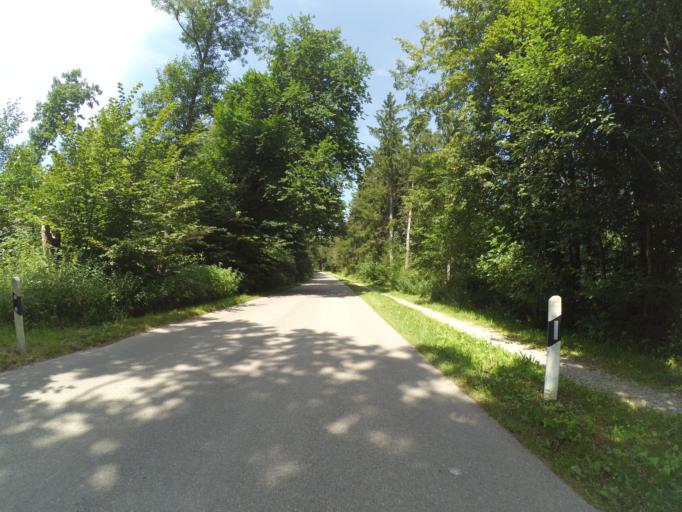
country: DE
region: Bavaria
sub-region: Swabia
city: Baisweil
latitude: 47.9815
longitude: 10.5694
